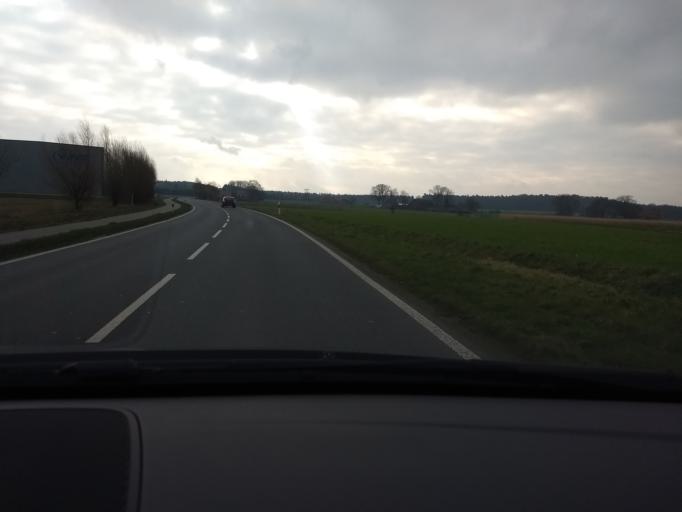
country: DE
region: North Rhine-Westphalia
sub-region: Regierungsbezirk Munster
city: Heiden
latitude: 51.8742
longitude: 6.9163
